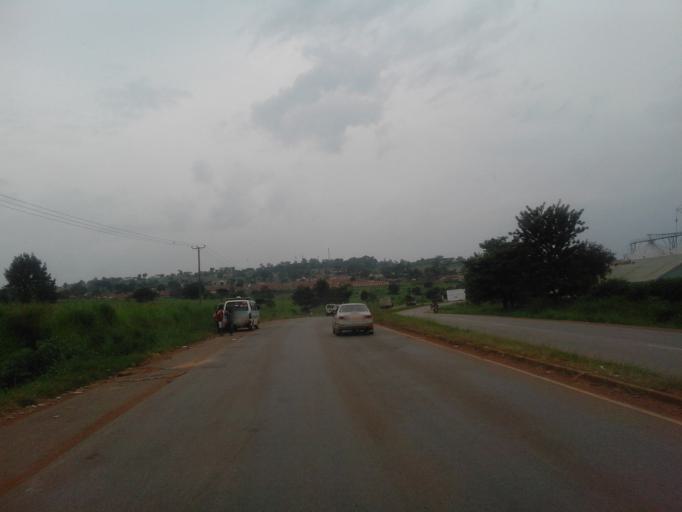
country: UG
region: Eastern Region
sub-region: Jinja District
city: Jinja
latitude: 0.4457
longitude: 33.1989
